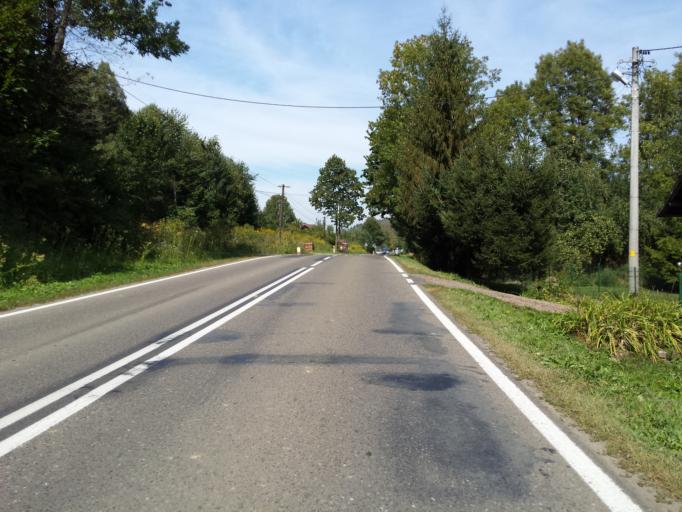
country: PL
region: Subcarpathian Voivodeship
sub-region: Powiat leski
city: Lesko
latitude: 49.4490
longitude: 22.3469
